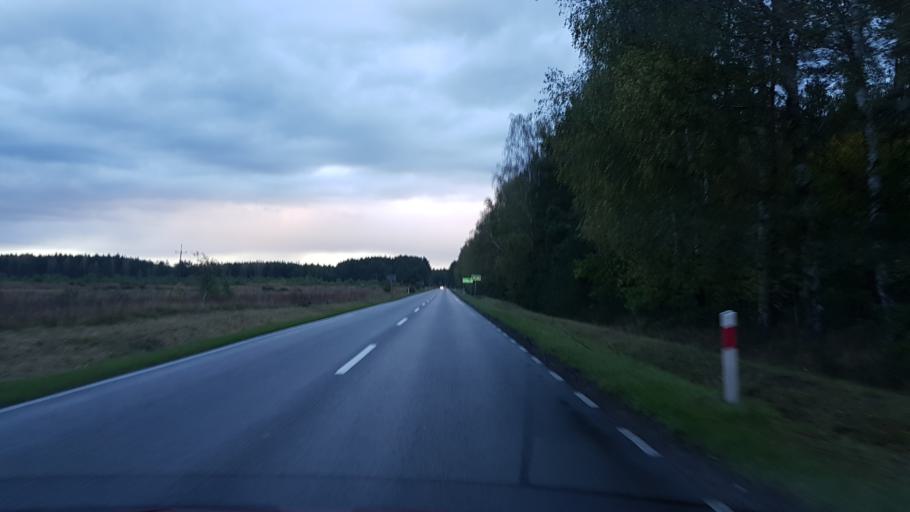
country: PL
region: Greater Poland Voivodeship
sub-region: Powiat pilski
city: Smilowo
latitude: 53.2288
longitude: 16.8772
